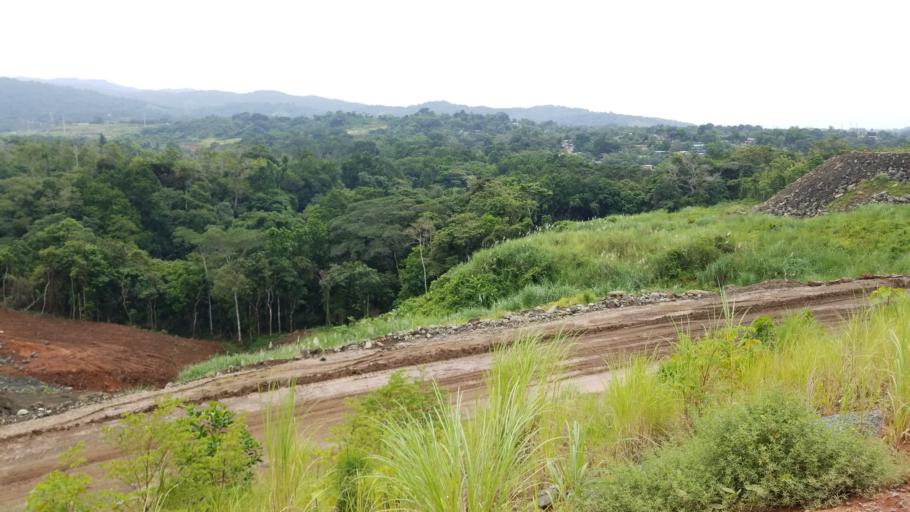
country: PA
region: Panama
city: San Miguelito
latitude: 9.0960
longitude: -79.4660
